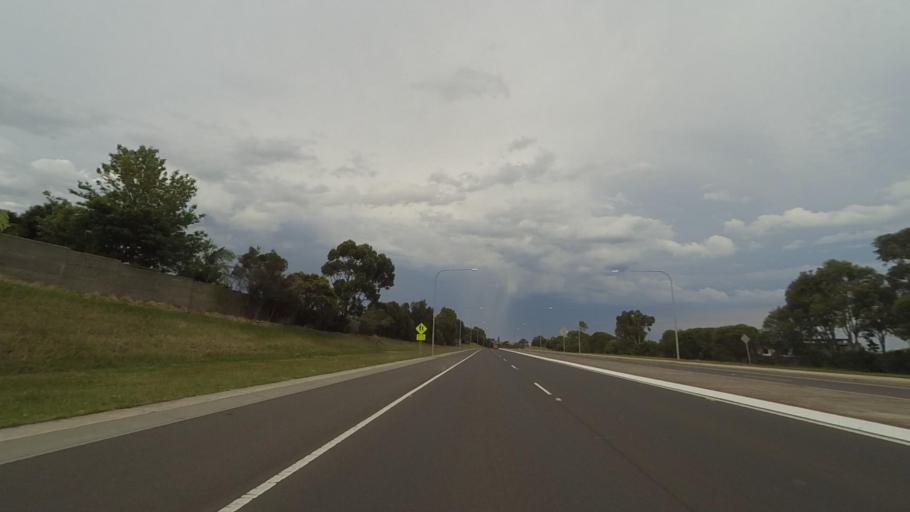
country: AU
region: New South Wales
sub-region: Shellharbour
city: Flinders
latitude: -34.5871
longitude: 150.8541
